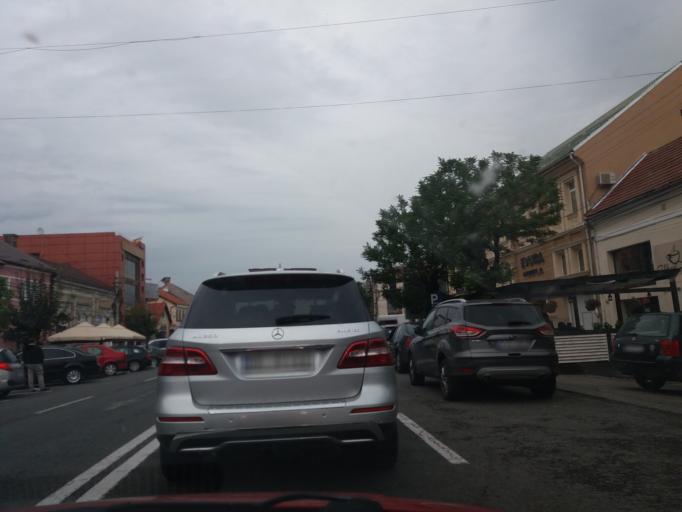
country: RO
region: Mures
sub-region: Municipiul Reghin
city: Reghin
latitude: 46.7781
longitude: 24.6992
